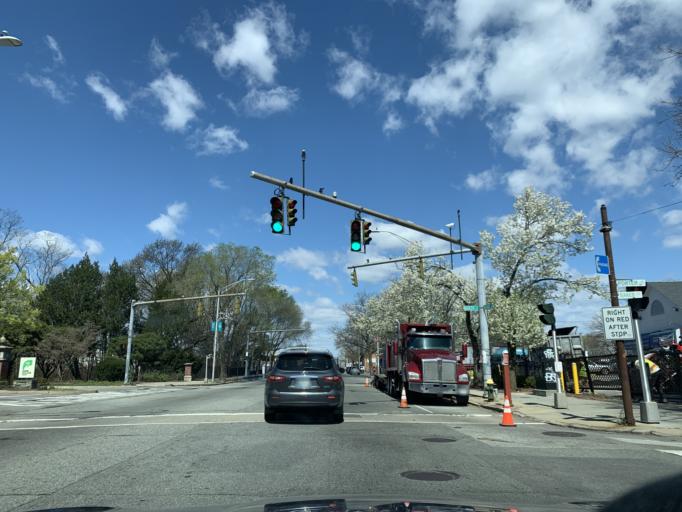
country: US
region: Rhode Island
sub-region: Providence County
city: Providence
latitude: 41.7927
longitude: -71.4078
